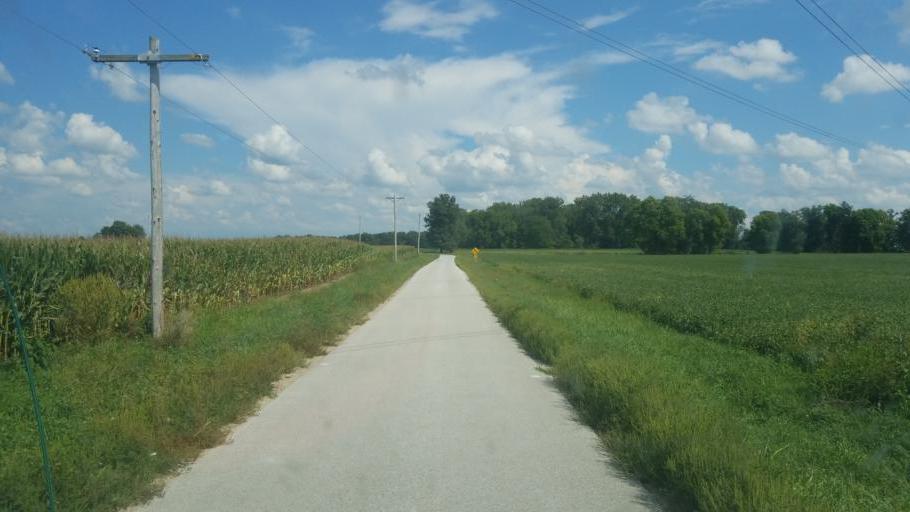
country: US
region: Ohio
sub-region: Wyandot County
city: Carey
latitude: 40.9710
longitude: -83.2446
